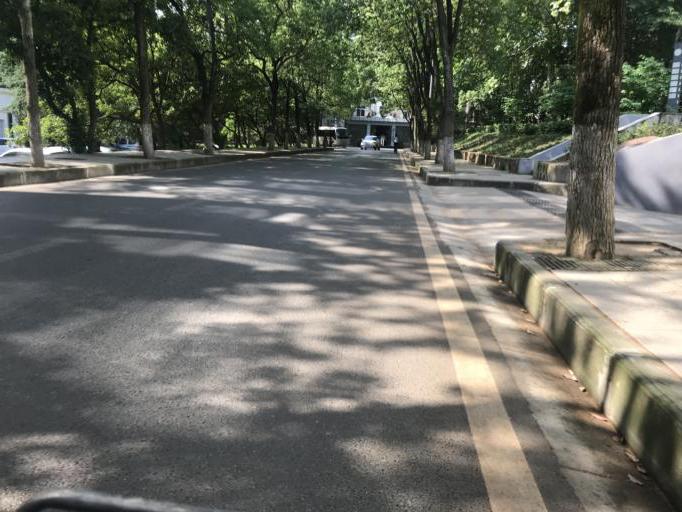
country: CN
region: Hubei
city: Shizishan
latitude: 30.5314
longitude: 114.3551
